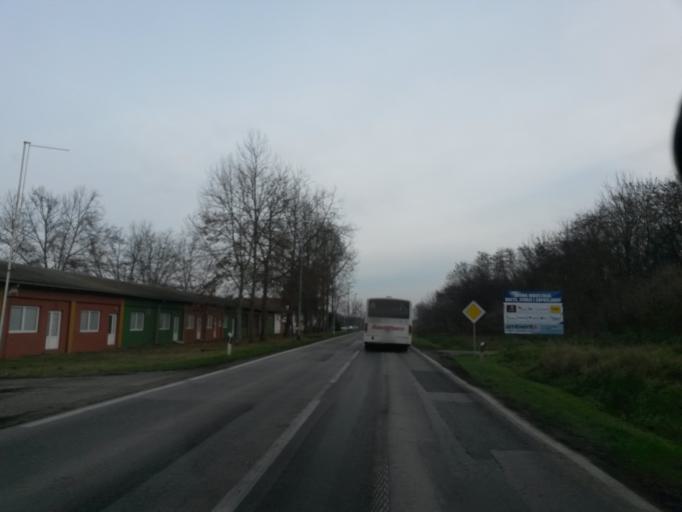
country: HR
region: Vukovarsko-Srijemska
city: Borovo
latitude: 45.3695
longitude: 18.9464
